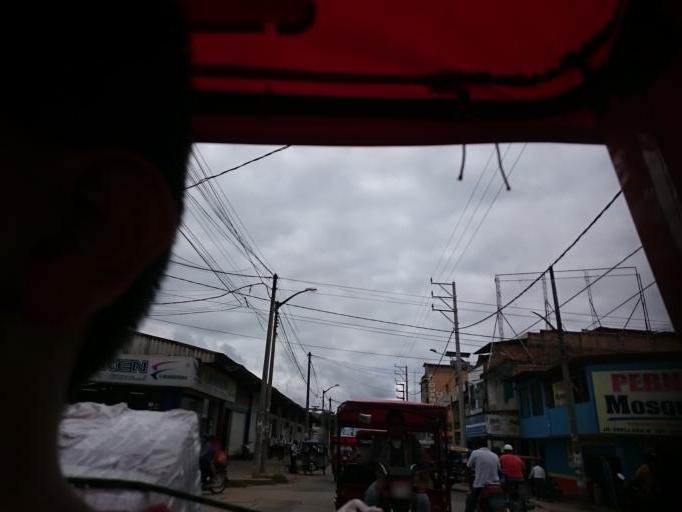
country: PE
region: San Martin
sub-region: Provincia de San Martin
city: Tarapoto
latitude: -6.4903
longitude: -76.3650
